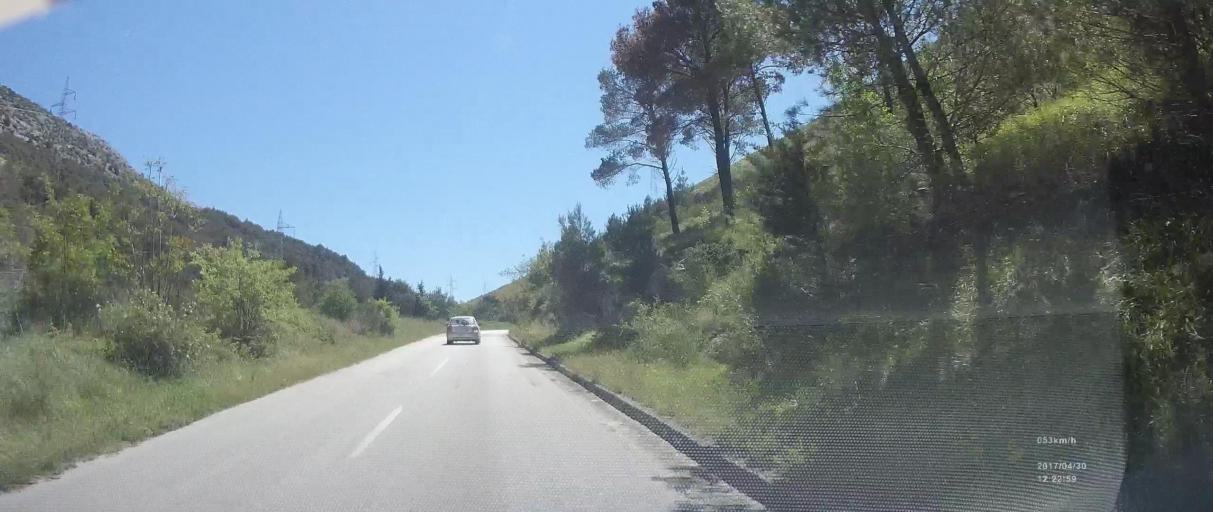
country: HR
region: Splitsko-Dalmatinska
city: Zrnovnica
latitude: 43.5184
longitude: 16.5746
